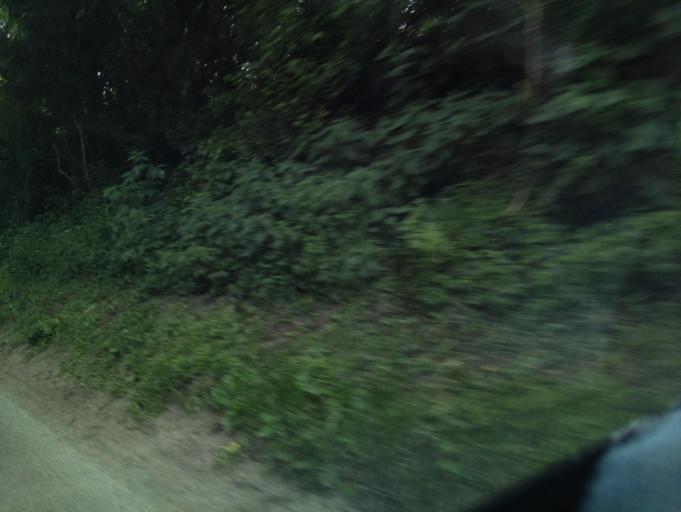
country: GB
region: England
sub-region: Herefordshire
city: Ross on Wye
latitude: 51.9363
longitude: -2.5592
